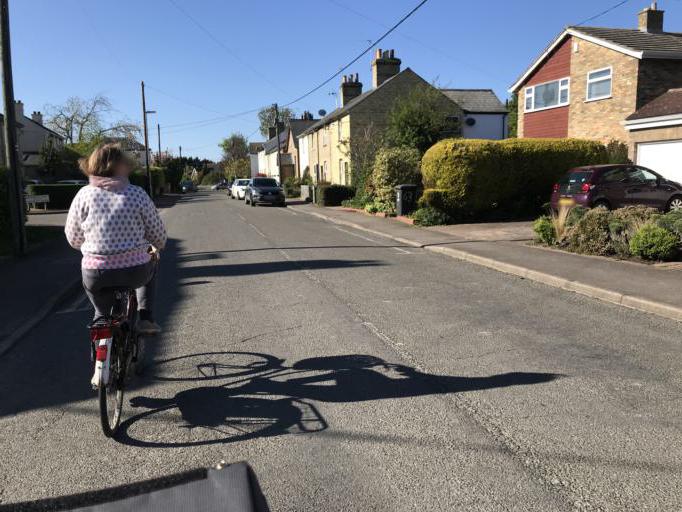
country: GB
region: England
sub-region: Cambridgeshire
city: Fulbourn
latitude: 52.2007
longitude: 0.1940
